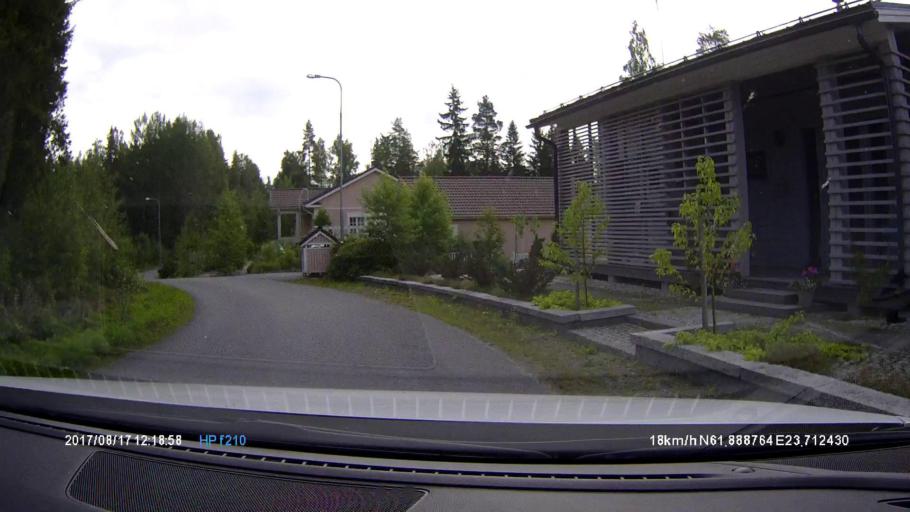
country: FI
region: Pirkanmaa
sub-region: Tampere
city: Kuru
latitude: 61.8885
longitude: 23.7129
